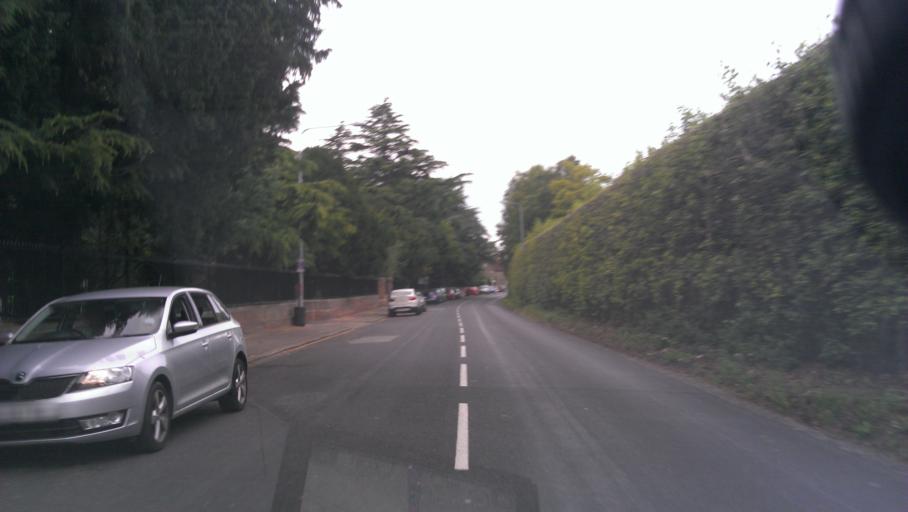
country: GB
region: England
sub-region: Kent
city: Faversham
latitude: 51.3100
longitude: 0.9052
